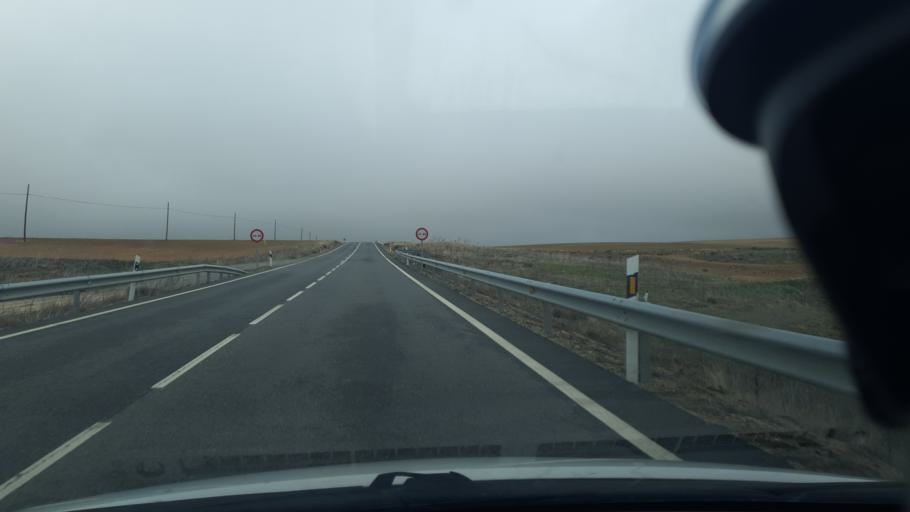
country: ES
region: Castille and Leon
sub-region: Provincia de Segovia
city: Encinillas
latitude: 41.0376
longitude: -4.1373
